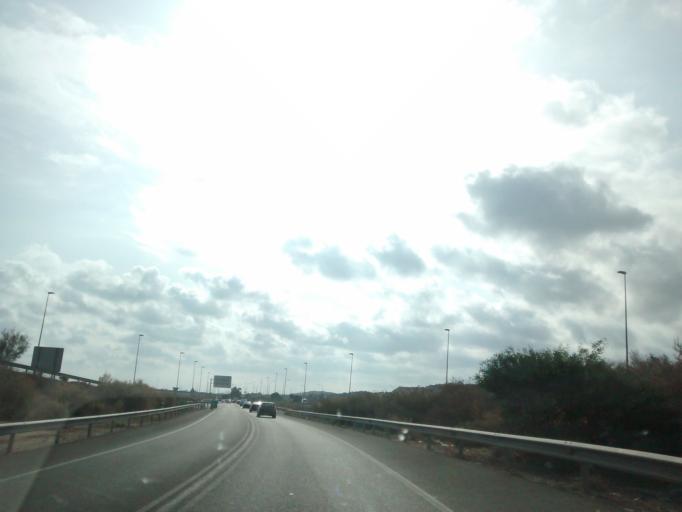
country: ES
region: Valencia
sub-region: Provincia de Alicante
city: el Campello
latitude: 38.4436
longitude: -0.3902
